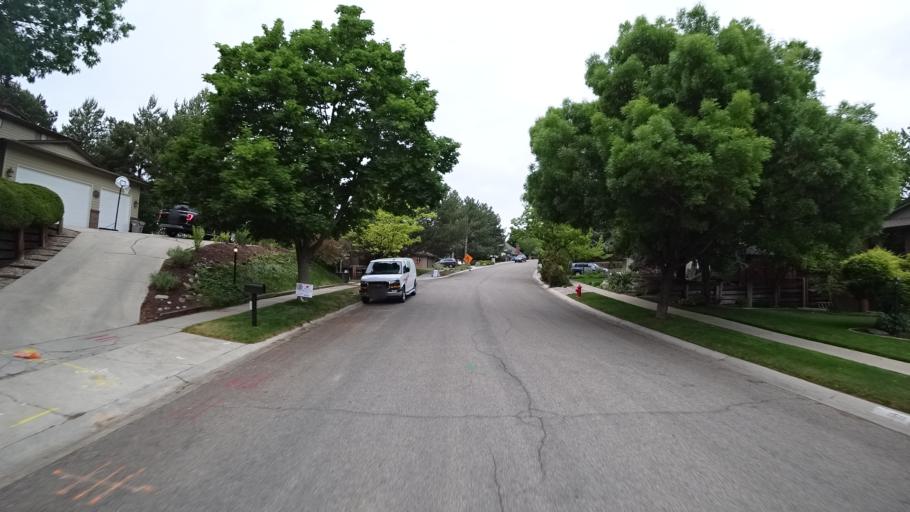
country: US
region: Idaho
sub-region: Ada County
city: Boise
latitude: 43.6145
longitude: -116.1714
